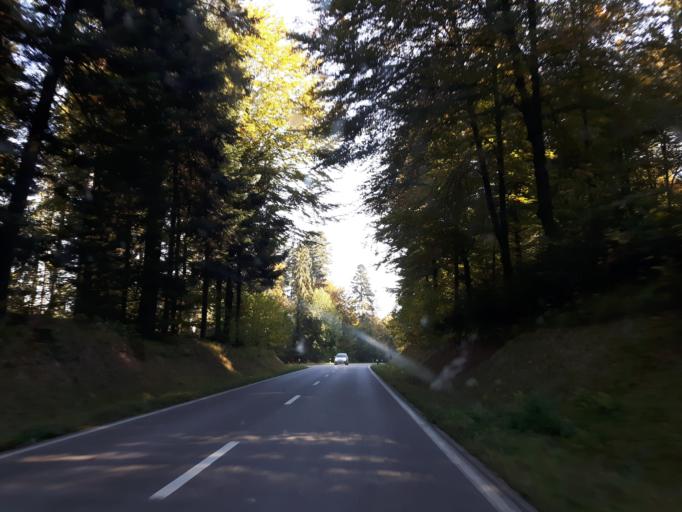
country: CH
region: Bern
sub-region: Oberaargau
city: Roggwil
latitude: 47.2491
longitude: 7.8449
